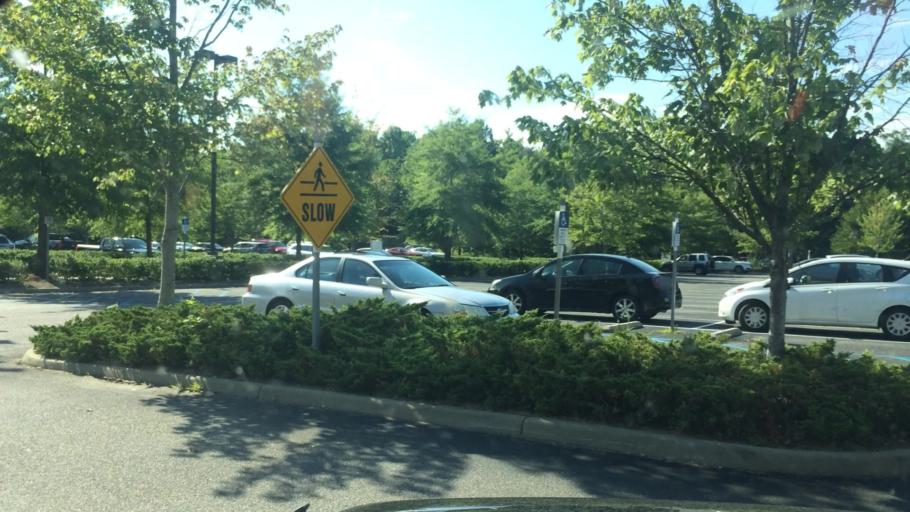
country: US
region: Virginia
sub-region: James City County
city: Williamsburg
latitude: 37.3378
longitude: -76.7415
